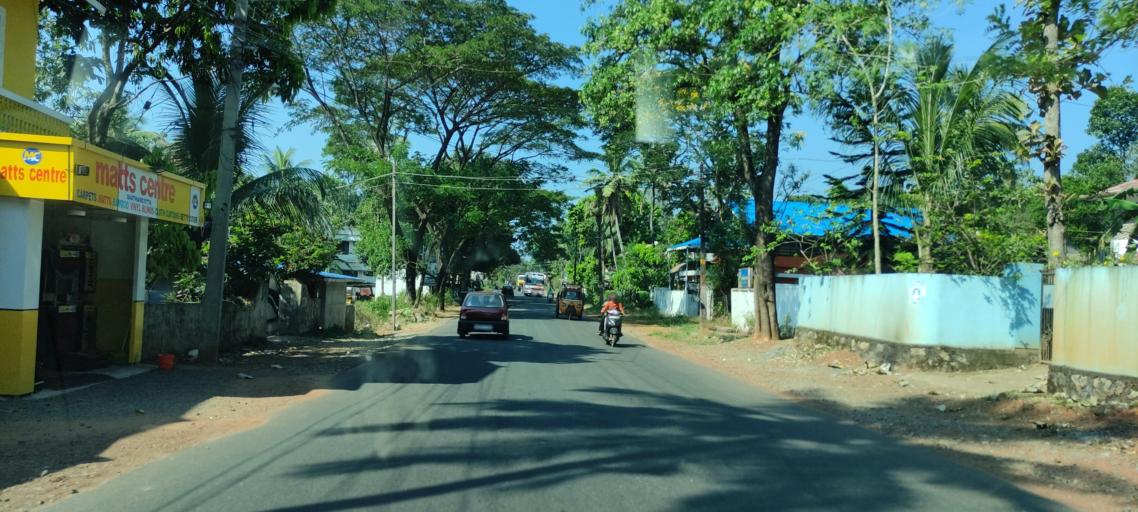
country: IN
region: Kerala
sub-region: Kollam
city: Panmana
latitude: 9.0432
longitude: 76.6201
